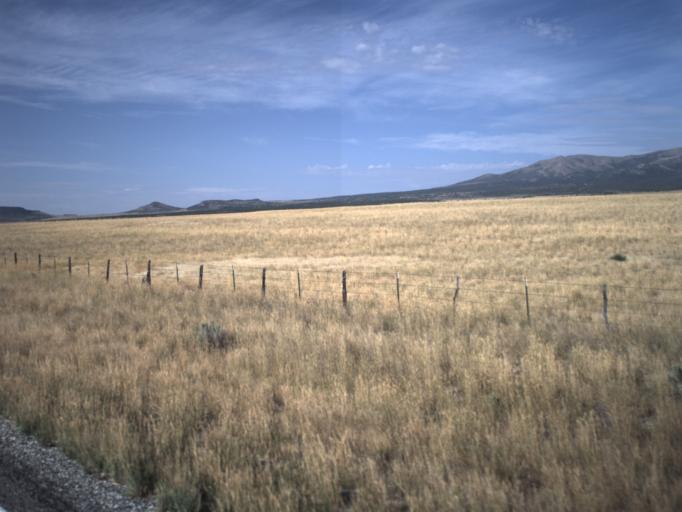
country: US
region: Idaho
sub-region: Oneida County
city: Malad City
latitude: 41.9083
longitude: -113.1022
